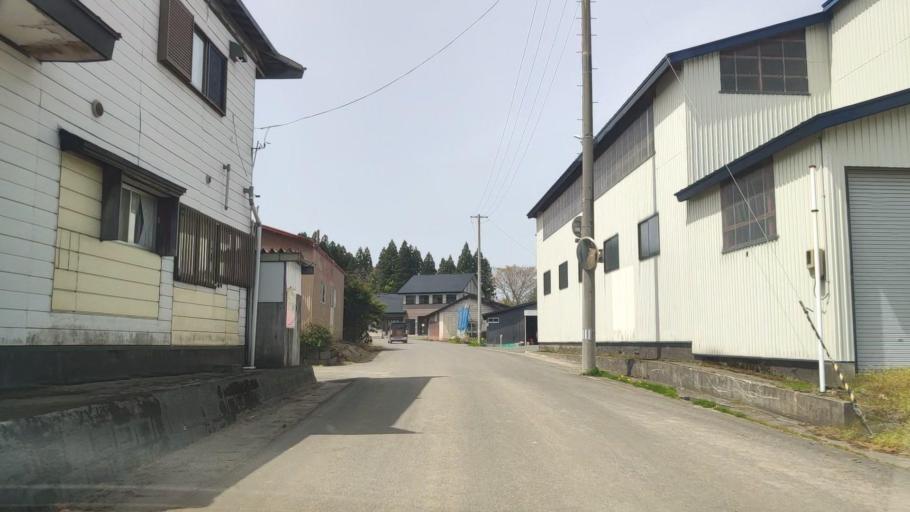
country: JP
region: Aomori
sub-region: Misawa Shi
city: Inuotose
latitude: 40.7795
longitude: 141.1222
